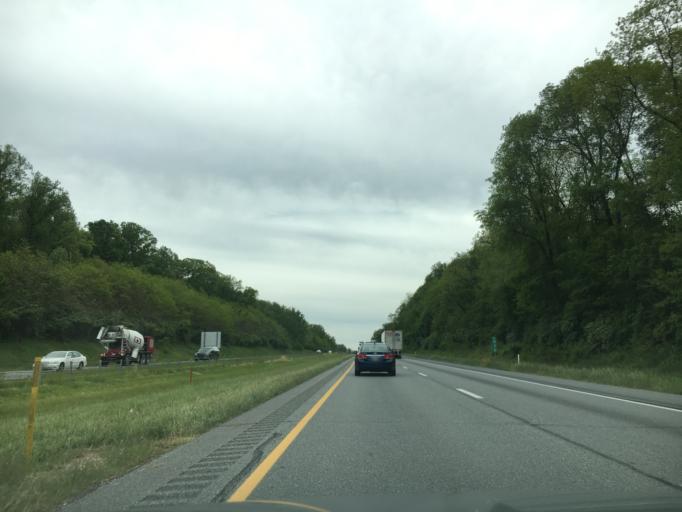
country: US
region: Pennsylvania
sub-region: Lancaster County
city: Reamstown
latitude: 40.1983
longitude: -76.1217
